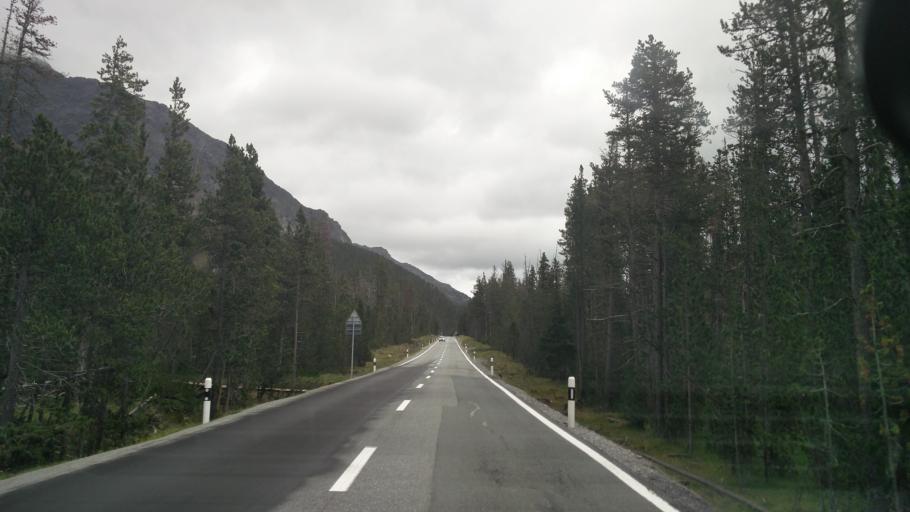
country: CH
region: Grisons
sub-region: Inn District
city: Zernez
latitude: 46.6605
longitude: 10.2317
